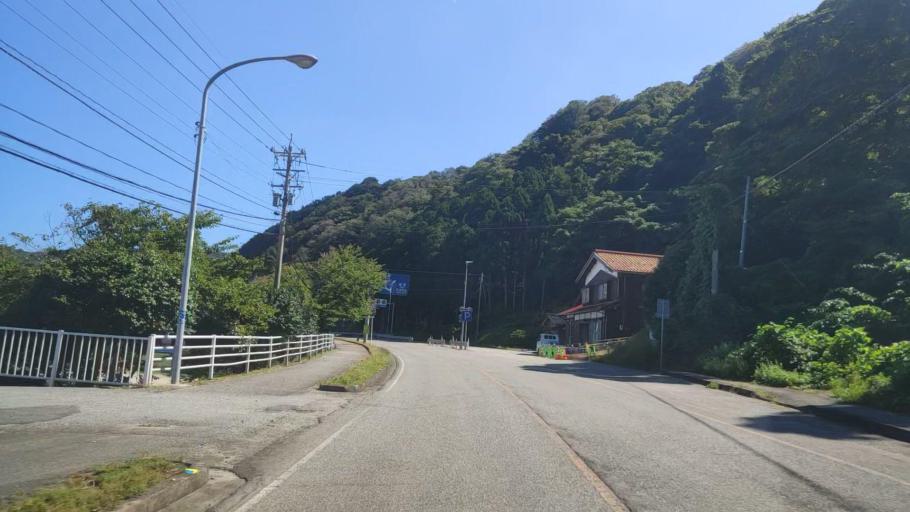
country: JP
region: Ishikawa
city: Nanao
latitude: 37.4993
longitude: 137.1765
